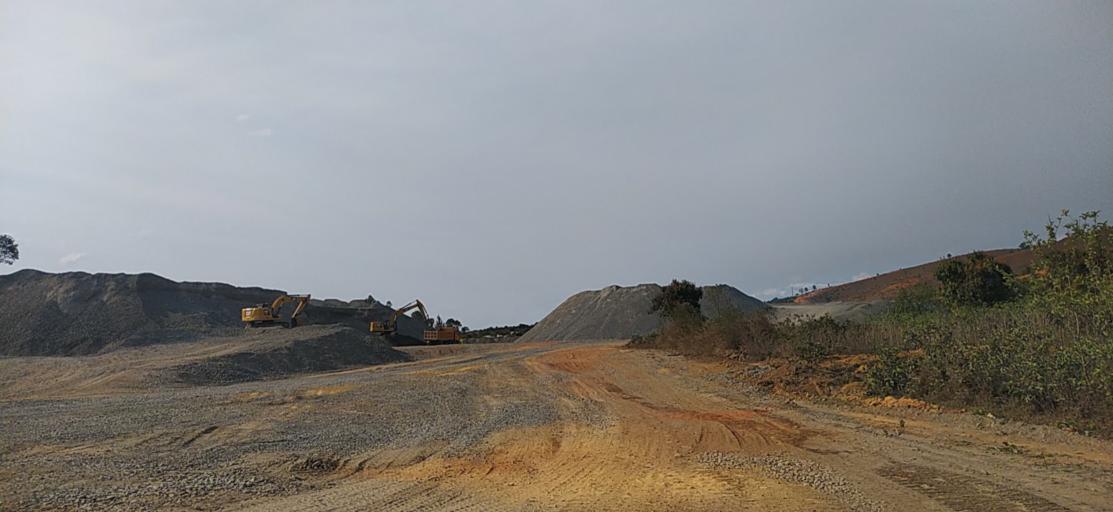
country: MG
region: Alaotra Mangoro
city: Moramanga
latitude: -18.6693
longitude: 48.2751
